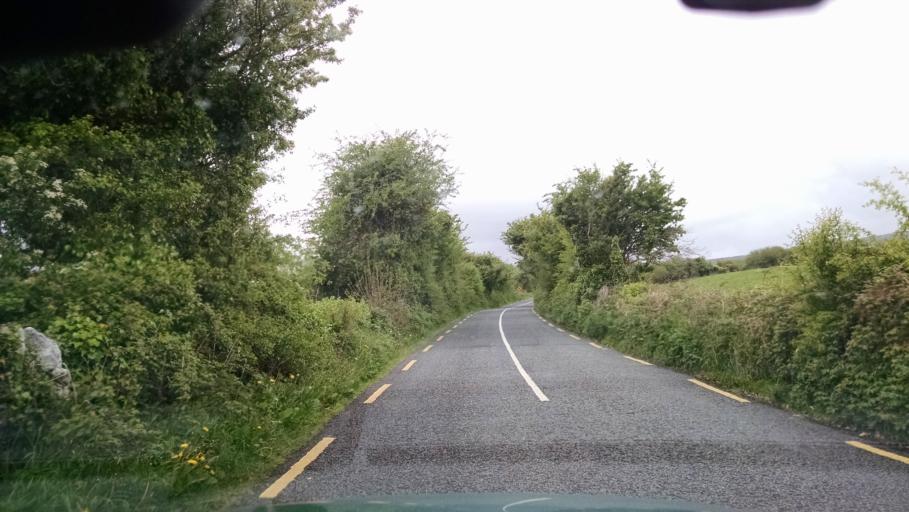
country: IE
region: Connaught
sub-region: County Galway
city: Bearna
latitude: 53.0869
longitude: -9.1615
